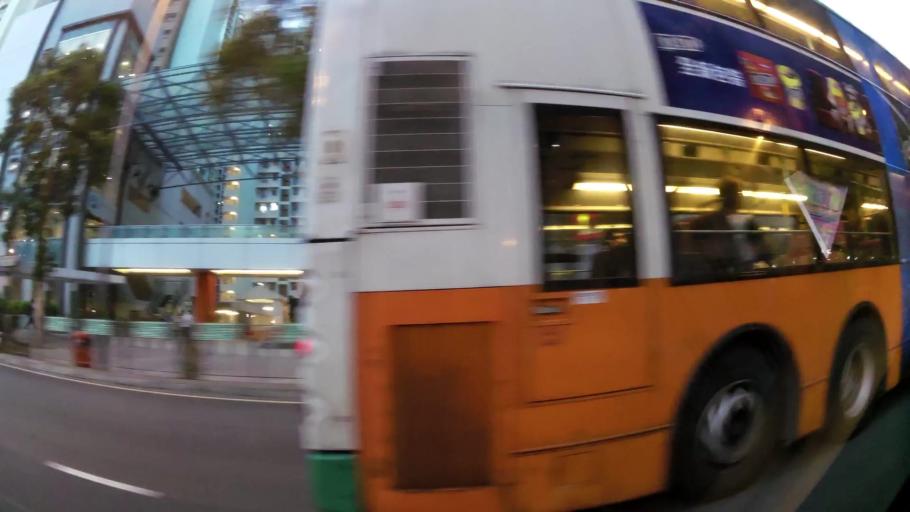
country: HK
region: Sham Shui Po
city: Sham Shui Po
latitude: 22.3276
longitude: 114.1544
